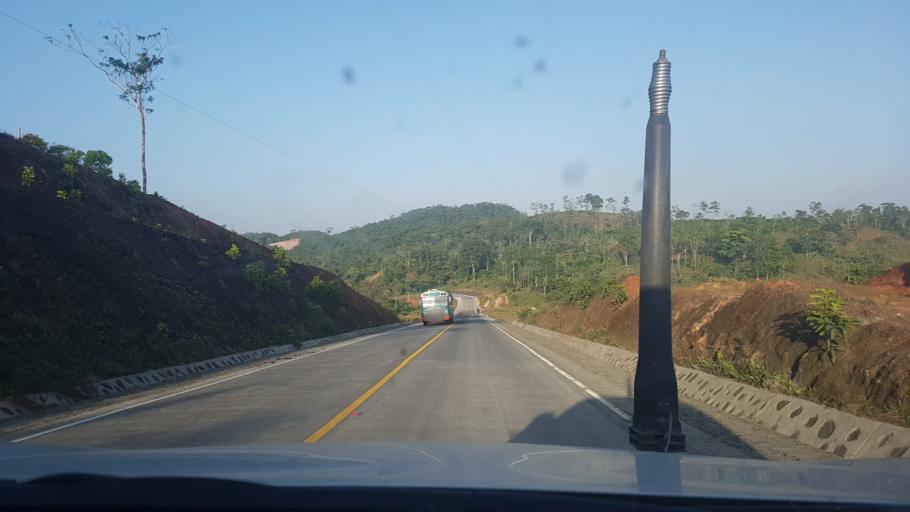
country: NI
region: Atlantico Sur
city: Rama
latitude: 11.8204
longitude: -84.0912
